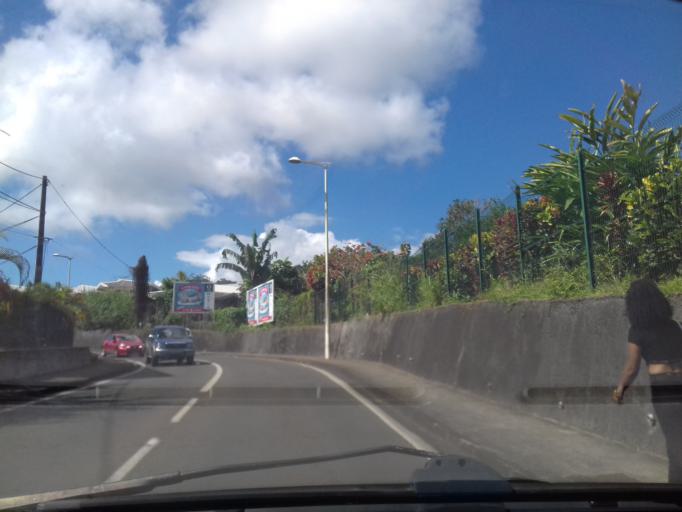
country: MQ
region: Martinique
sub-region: Martinique
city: Saint-Joseph
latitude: 14.6732
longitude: -61.0307
